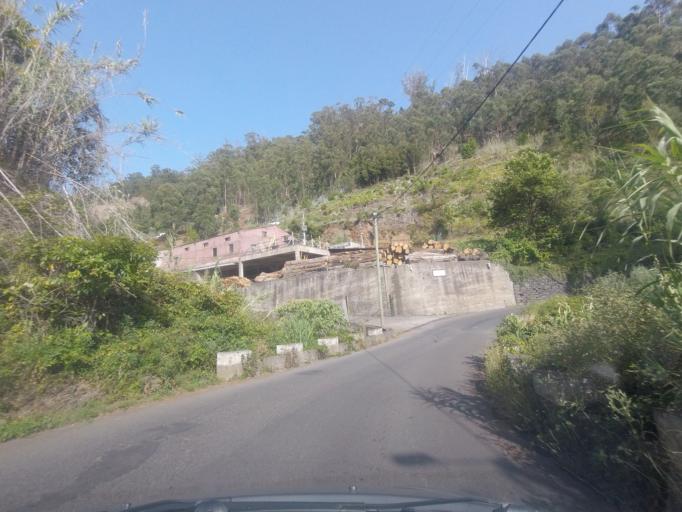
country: PT
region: Madeira
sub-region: Calheta
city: Arco da Calheta
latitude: 32.7257
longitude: -17.1513
